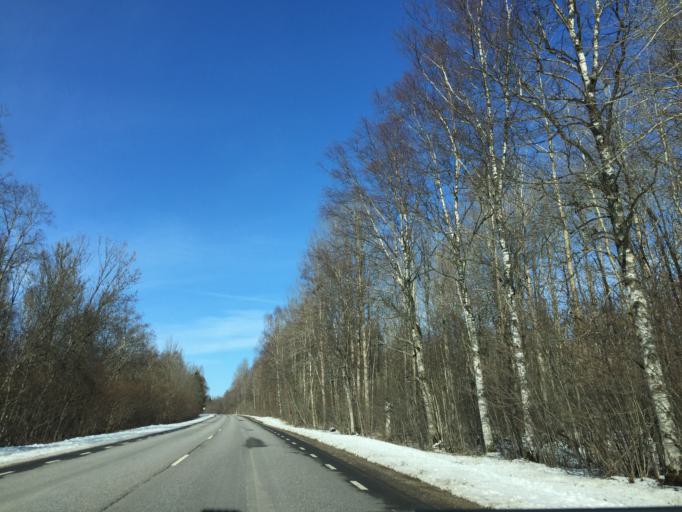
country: EE
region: Laeaene
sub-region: Lihula vald
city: Lihula
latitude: 58.6211
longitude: 23.6920
